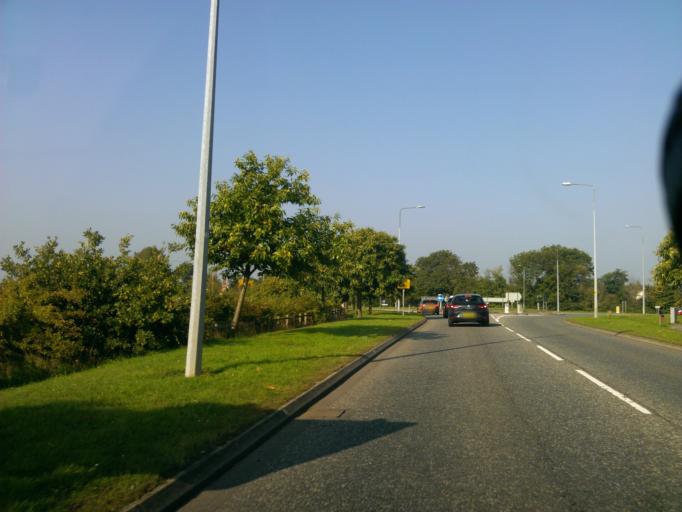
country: GB
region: England
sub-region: Essex
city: Layer de la Haye
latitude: 51.8697
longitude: 0.8583
